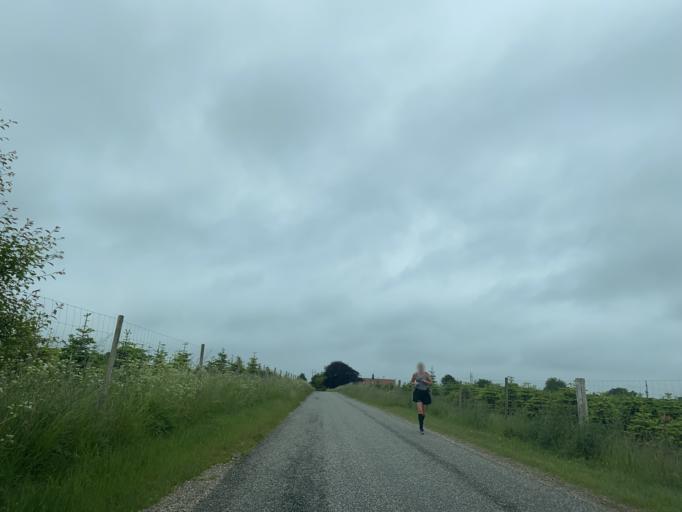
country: DK
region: Central Jutland
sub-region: Viborg Kommune
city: Bjerringbro
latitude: 56.3496
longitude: 9.6313
